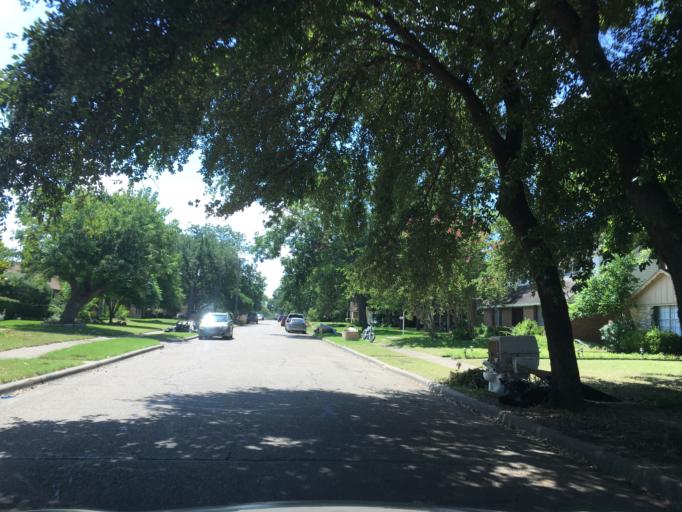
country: US
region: Texas
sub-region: Dallas County
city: Garland
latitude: 32.8455
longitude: -96.6602
